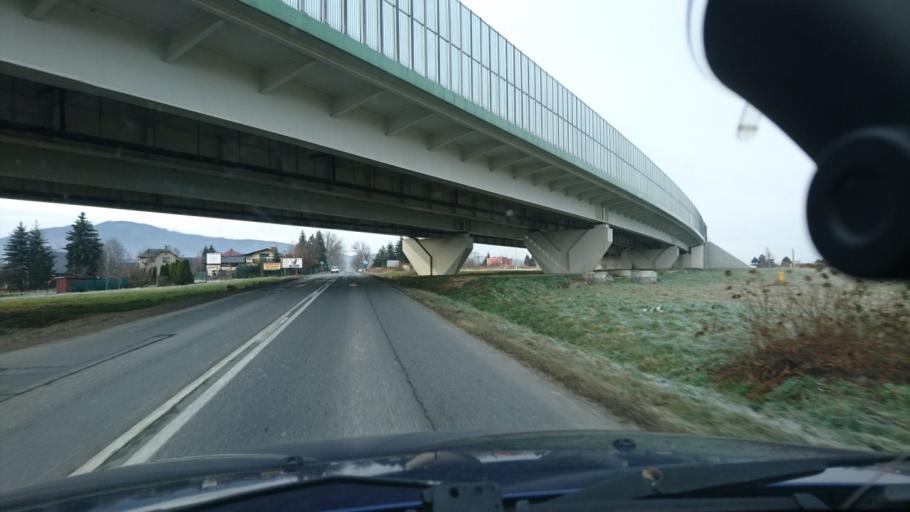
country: PL
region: Silesian Voivodeship
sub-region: Powiat bielski
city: Rybarzowice
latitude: 49.7339
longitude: 19.1153
